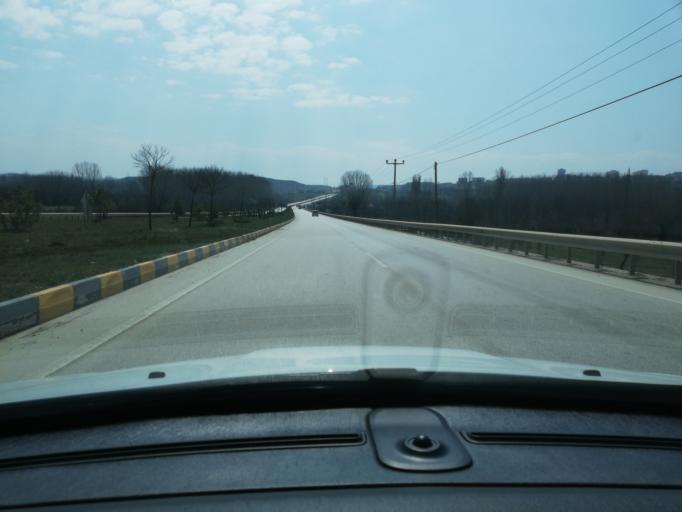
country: TR
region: Kastamonu
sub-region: Cide
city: Kastamonu
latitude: 41.4475
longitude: 33.7930
